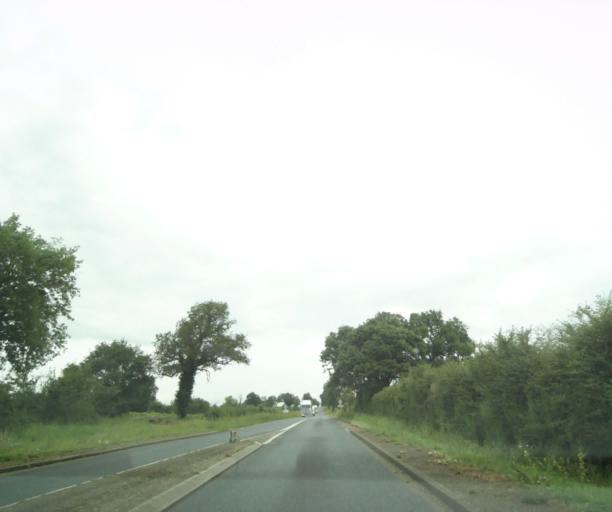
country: FR
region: Poitou-Charentes
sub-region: Departement des Deux-Sevres
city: Viennay
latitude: 46.7343
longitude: -0.2356
